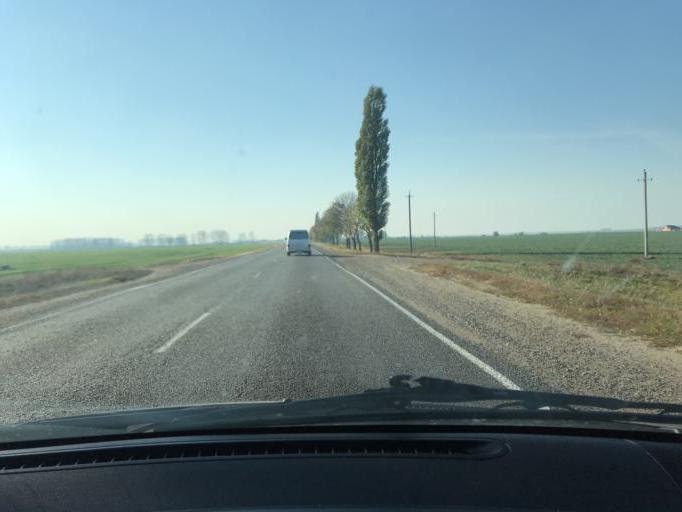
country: BY
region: Brest
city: Davyd-Haradok
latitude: 52.0640
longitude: 27.3188
